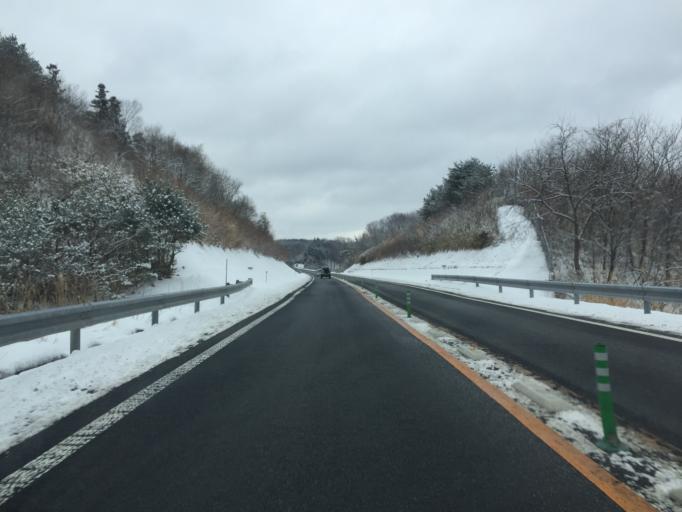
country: JP
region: Fukushima
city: Ishikawa
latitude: 37.2600
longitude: 140.5663
